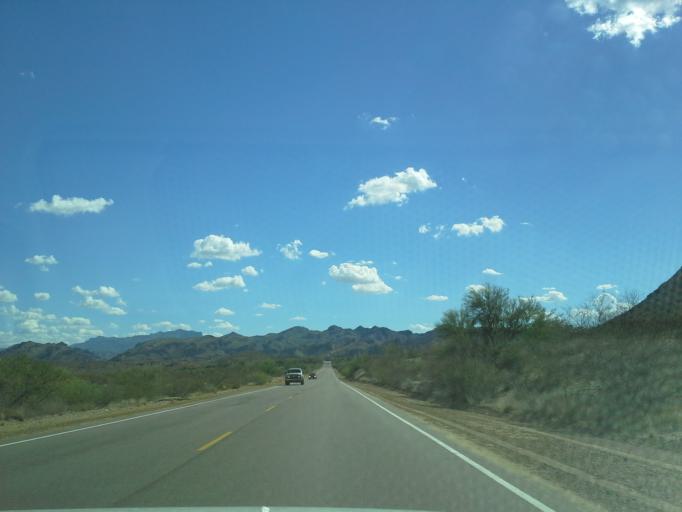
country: US
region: Arizona
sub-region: Maricopa County
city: Fountain Hills
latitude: 33.5986
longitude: -111.5455
